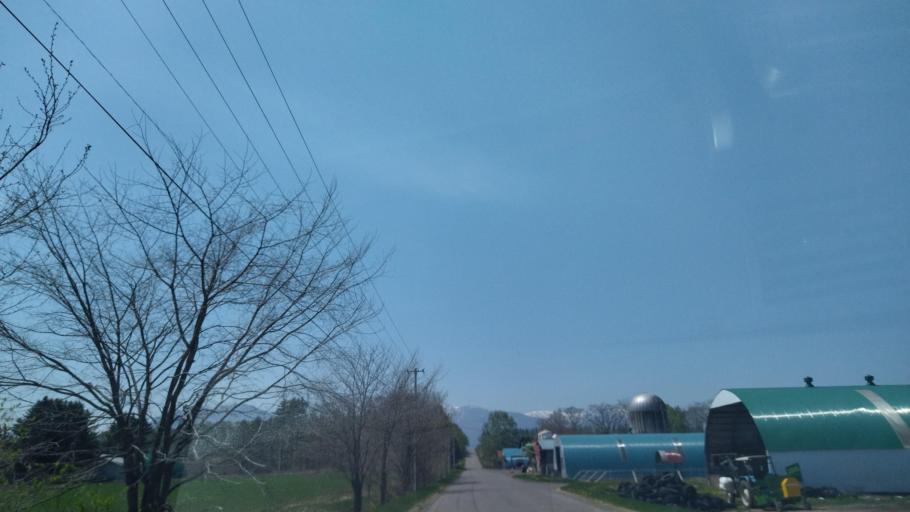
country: JP
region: Hokkaido
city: Obihiro
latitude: 42.8939
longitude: 143.0227
